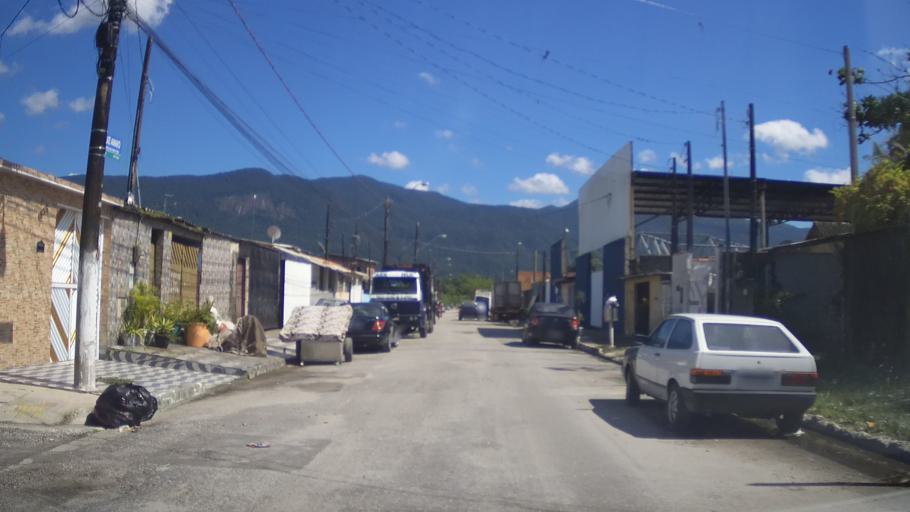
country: BR
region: Sao Paulo
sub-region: Mongagua
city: Mongagua
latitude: -24.0313
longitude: -46.5356
